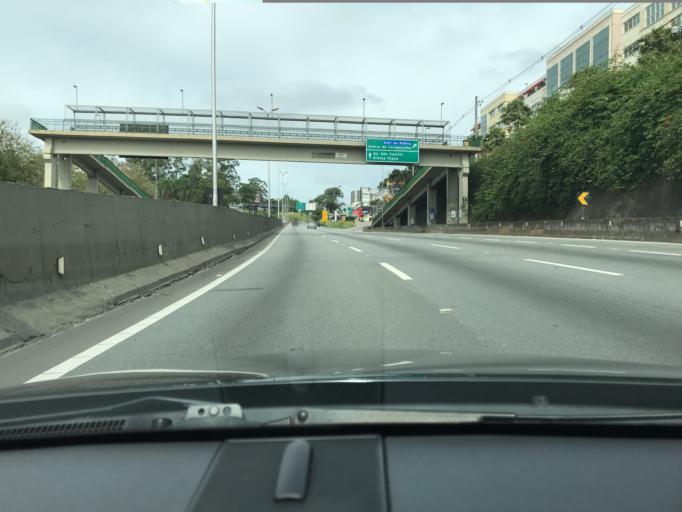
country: BR
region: Sao Paulo
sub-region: Taboao Da Serra
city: Taboao da Serra
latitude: -23.5906
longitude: -46.8234
